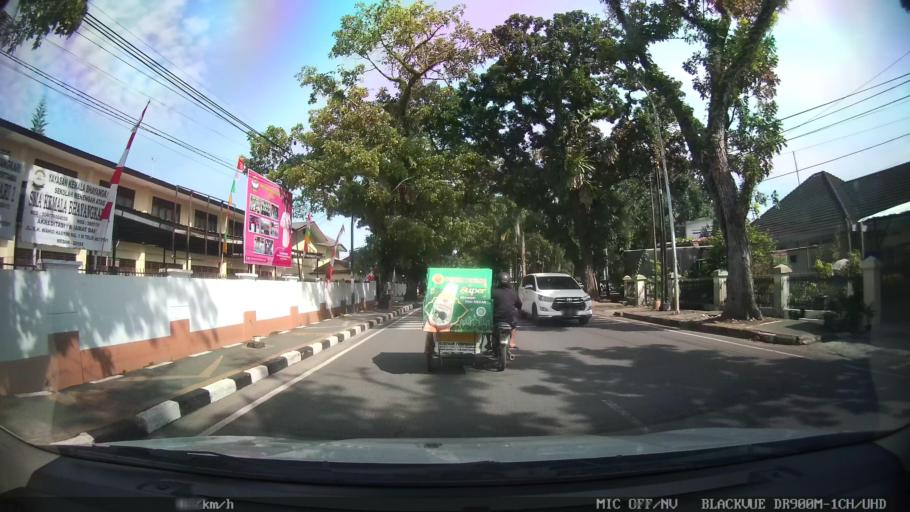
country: ID
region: North Sumatra
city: Medan
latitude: 3.5729
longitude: 98.6592
